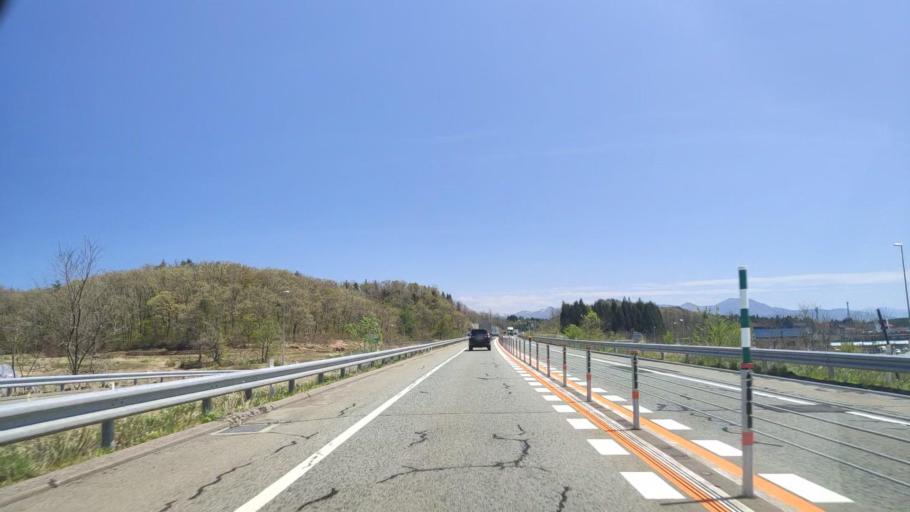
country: JP
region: Yamagata
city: Obanazawa
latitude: 38.6599
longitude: 140.3626
